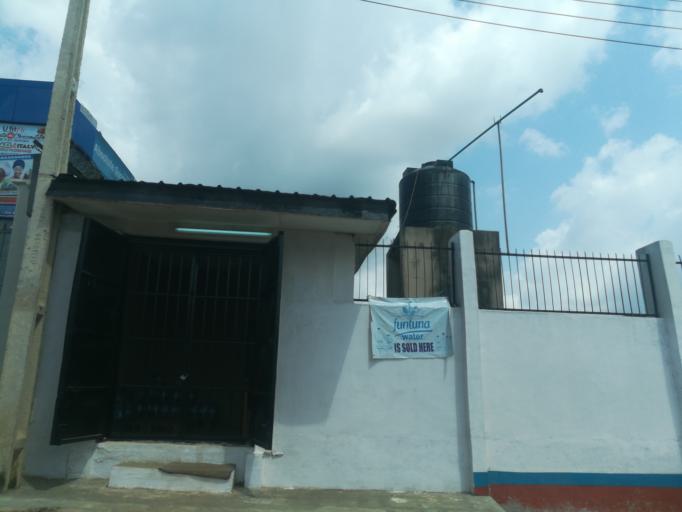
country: NG
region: Oyo
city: Ibadan
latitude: 7.3637
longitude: 3.8577
